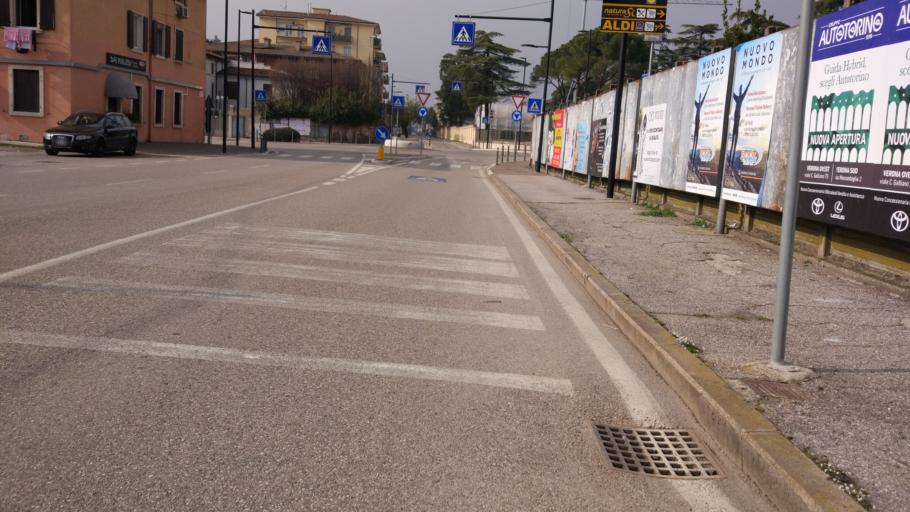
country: IT
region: Veneto
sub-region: Provincia di Verona
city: Villafranca di Verona
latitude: 45.3535
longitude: 10.8514
